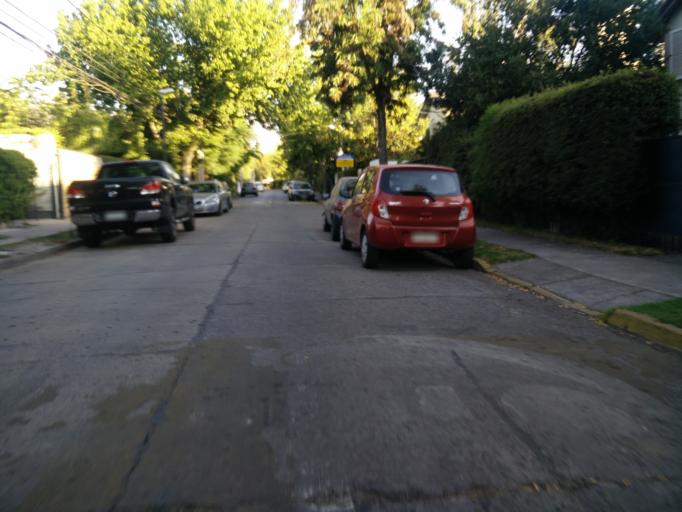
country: CL
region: Santiago Metropolitan
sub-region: Provincia de Santiago
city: Villa Presidente Frei, Nunoa, Santiago, Chile
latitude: -33.3911
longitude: -70.5897
